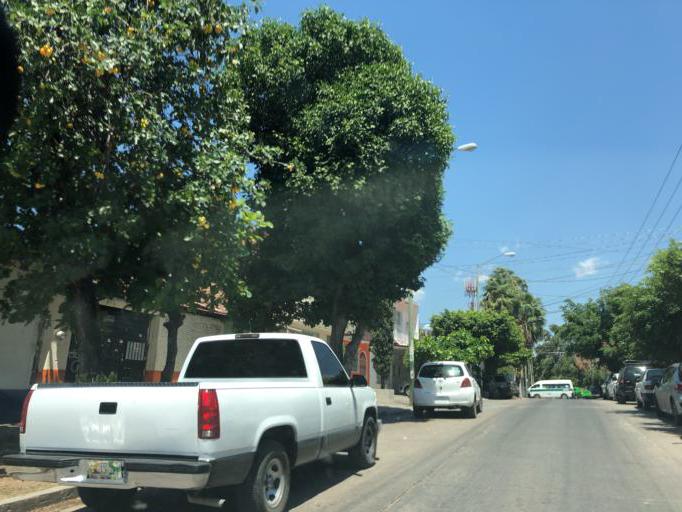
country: MX
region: Chiapas
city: Tuxtla Gutierrez
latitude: 16.7597
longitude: -93.1187
